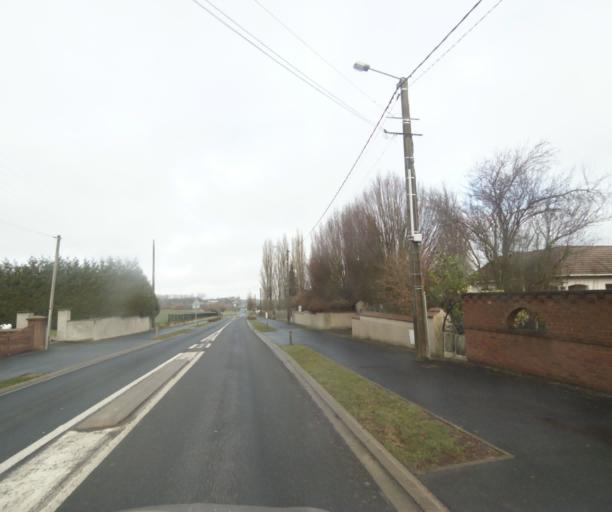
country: FR
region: Nord-Pas-de-Calais
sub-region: Departement du Nord
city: Famars
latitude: 50.2937
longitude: 3.5147
